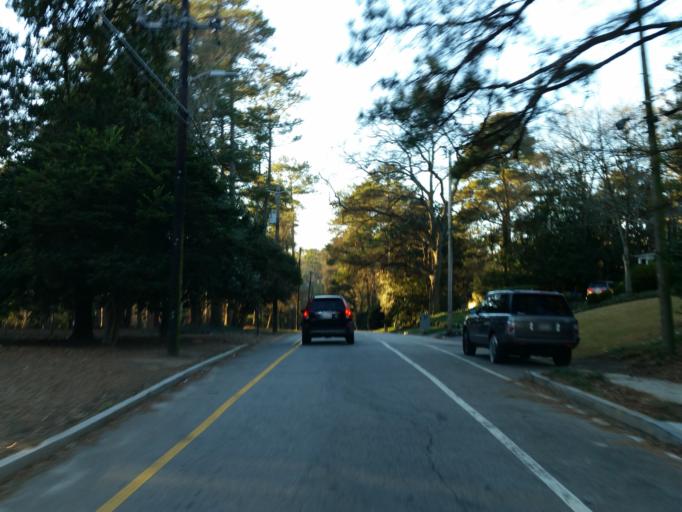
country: US
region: Georgia
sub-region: DeKalb County
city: Druid Hills
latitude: 33.8204
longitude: -84.3899
